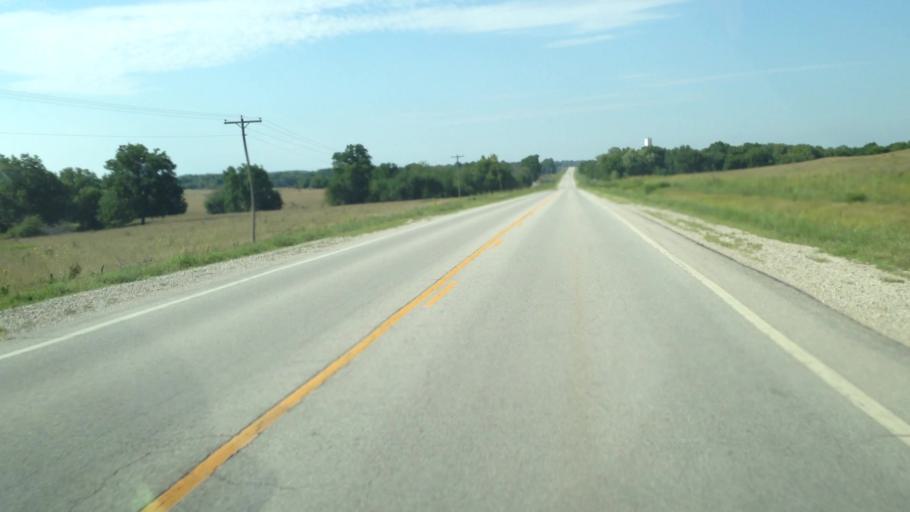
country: US
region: Kansas
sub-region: Neosho County
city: Erie
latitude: 37.5005
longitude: -95.2697
